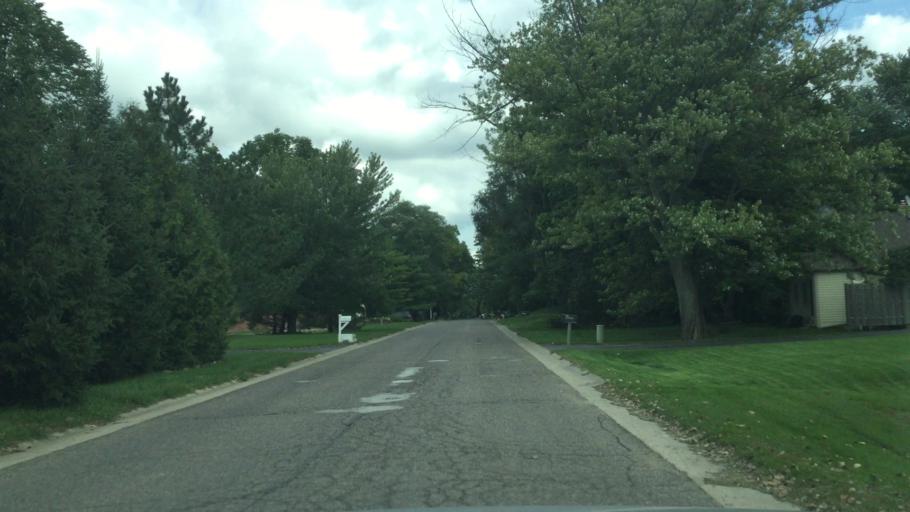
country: US
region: Michigan
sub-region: Livingston County
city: Brighton
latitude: 42.5565
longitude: -83.7535
